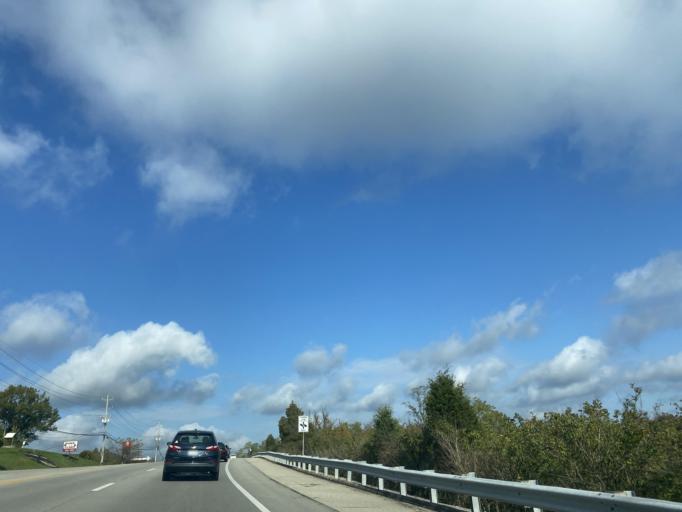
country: US
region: Kentucky
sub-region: Campbell County
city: Cold Spring
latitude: 38.9953
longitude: -84.4153
